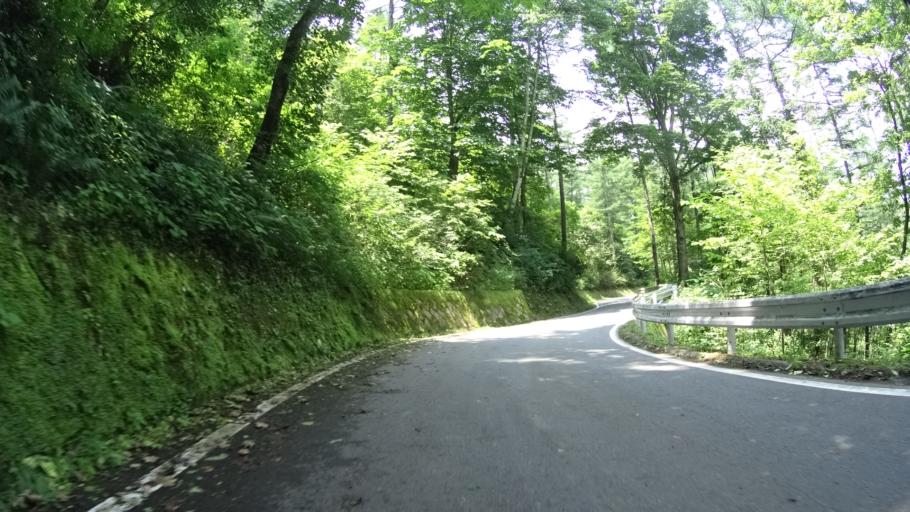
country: JP
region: Nagano
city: Saku
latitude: 36.0983
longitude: 138.6566
